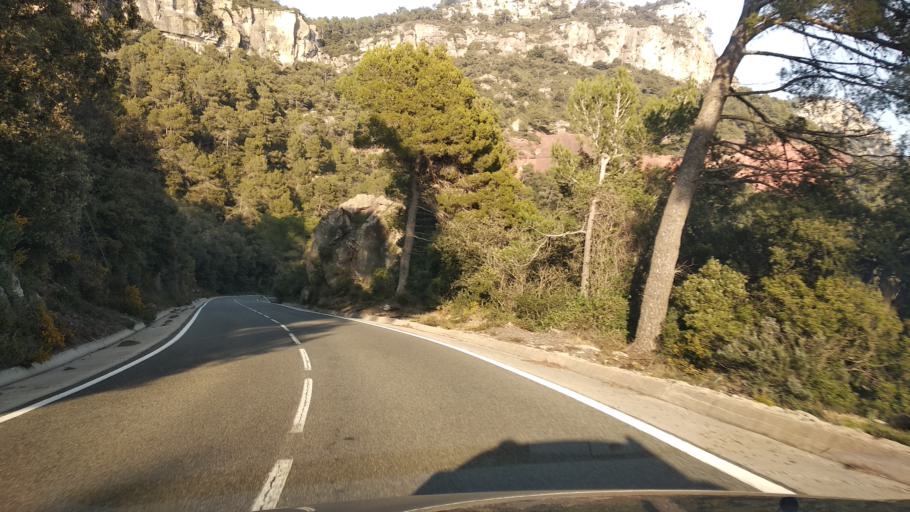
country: ES
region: Catalonia
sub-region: Provincia de Tarragona
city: Alforja
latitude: 41.2205
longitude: 0.9419
